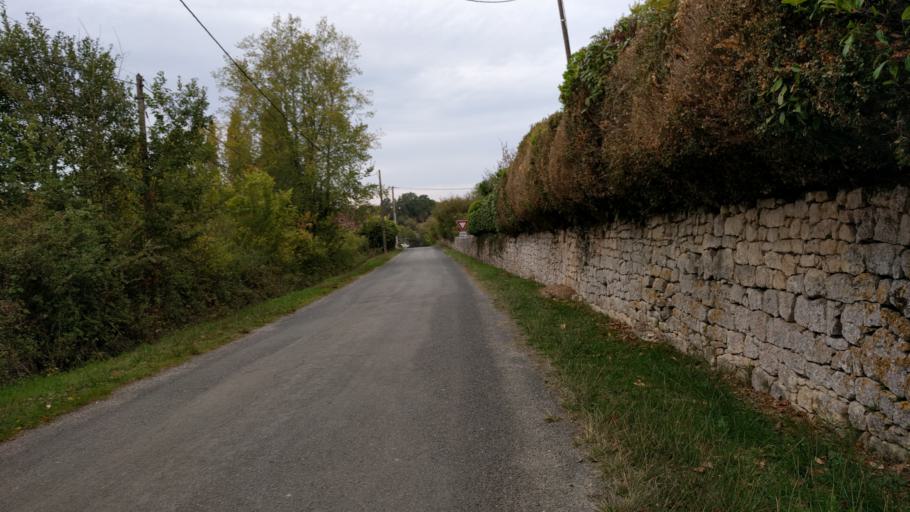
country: FR
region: Aquitaine
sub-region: Departement de la Dordogne
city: Mouleydier
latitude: 44.8968
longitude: 0.6486
